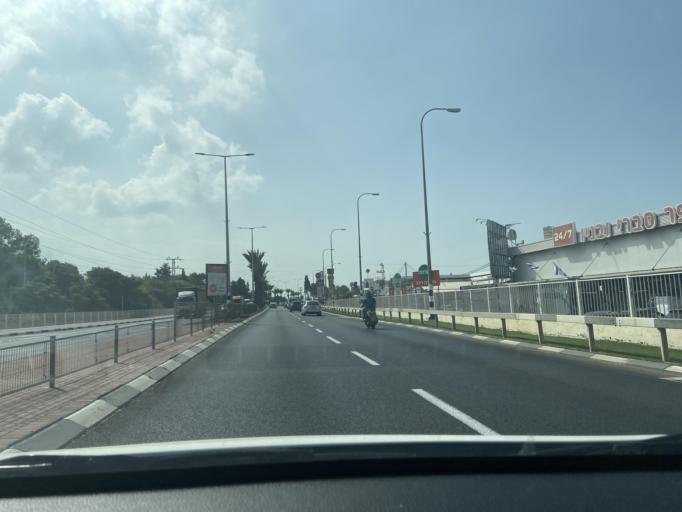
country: IL
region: Northern District
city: El Mazra`a
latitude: 32.9939
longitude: 35.0970
